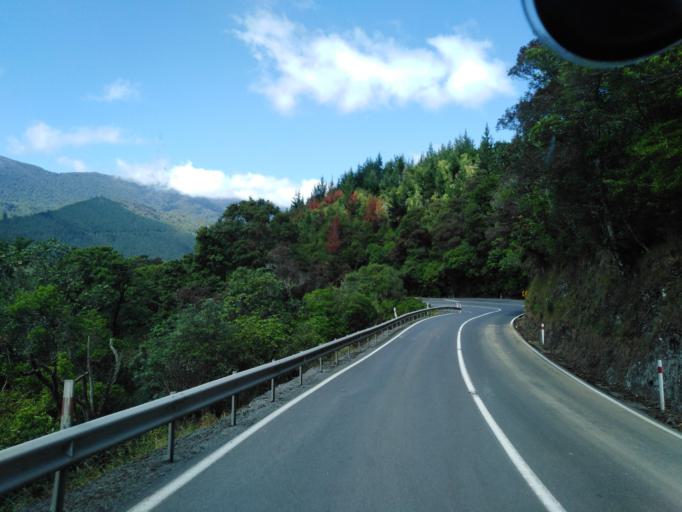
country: NZ
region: Nelson
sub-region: Nelson City
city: Nelson
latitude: -41.2236
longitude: 173.4358
